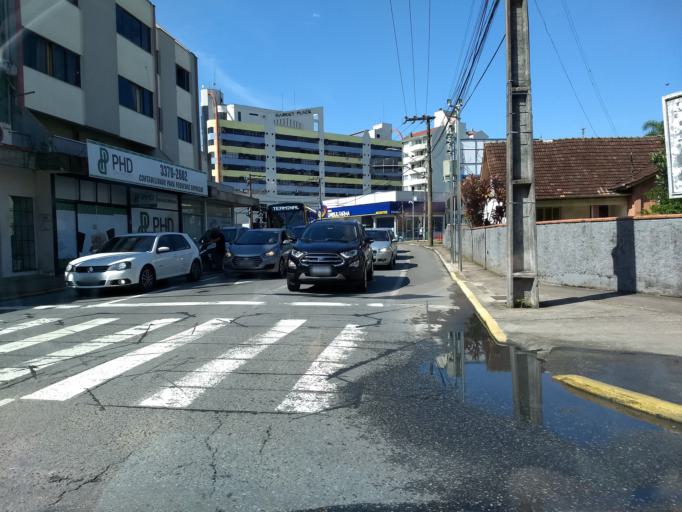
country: BR
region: Santa Catarina
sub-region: Jaragua Do Sul
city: Jaragua do Sul
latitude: -26.4834
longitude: -49.0803
